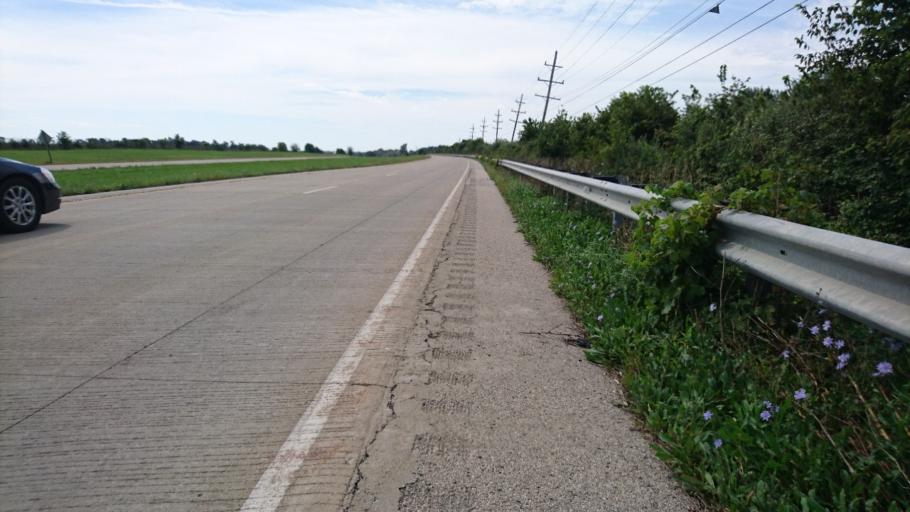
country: US
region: Illinois
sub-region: Will County
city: Elwood
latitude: 41.3748
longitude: -88.1305
